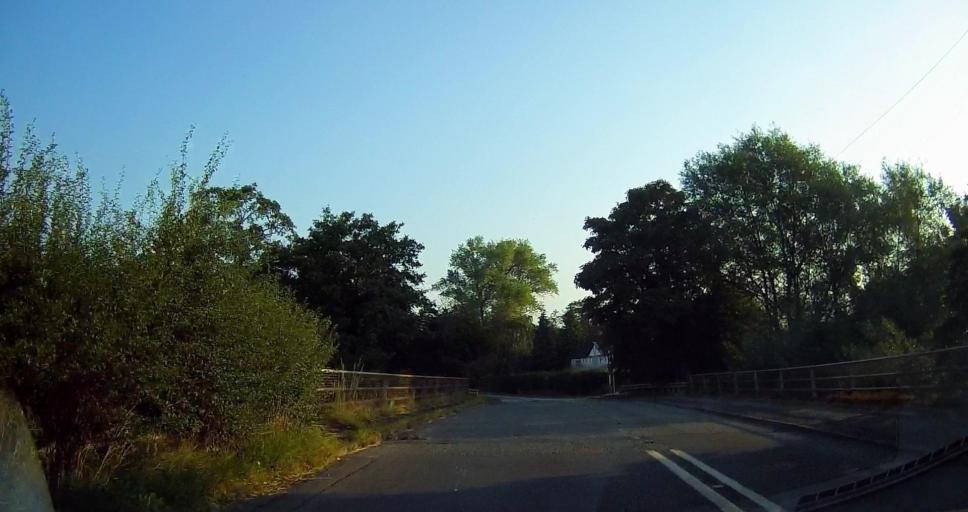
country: GB
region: England
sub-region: Cheshire East
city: Nantwich
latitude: 53.0542
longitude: -2.5246
